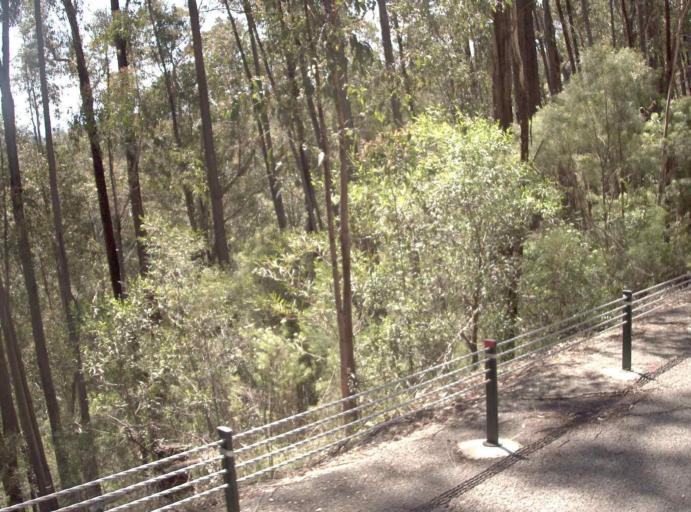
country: AU
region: New South Wales
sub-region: Bombala
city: Bombala
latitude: -37.5880
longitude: 148.9907
